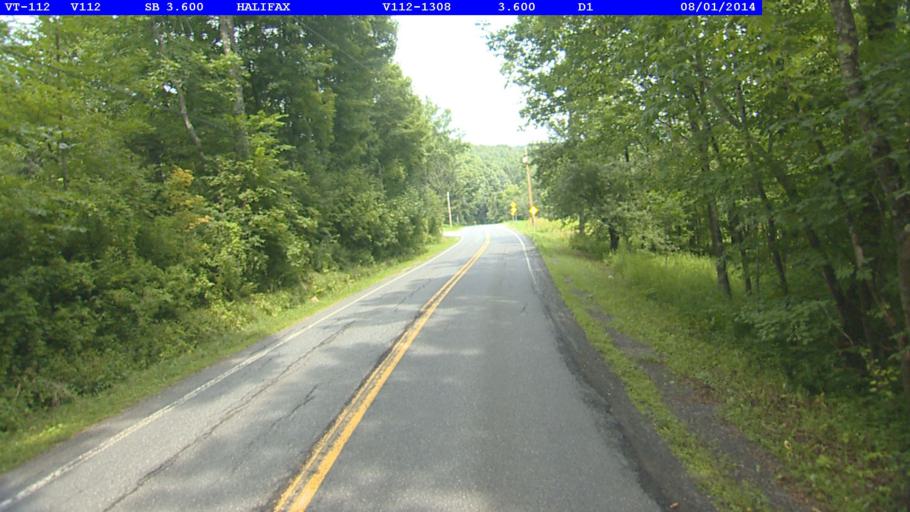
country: US
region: Massachusetts
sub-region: Franklin County
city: Colrain
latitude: 42.7620
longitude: -72.7748
